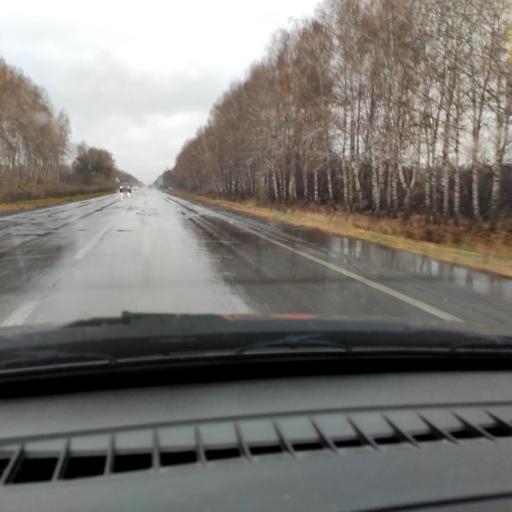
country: RU
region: Samara
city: Tol'yatti
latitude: 53.5937
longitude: 49.3272
